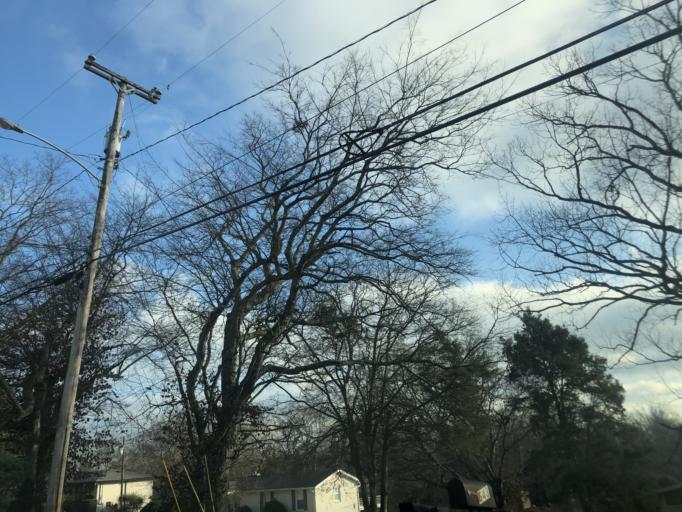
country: US
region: Tennessee
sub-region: Davidson County
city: Nashville
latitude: 36.2109
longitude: -86.8023
